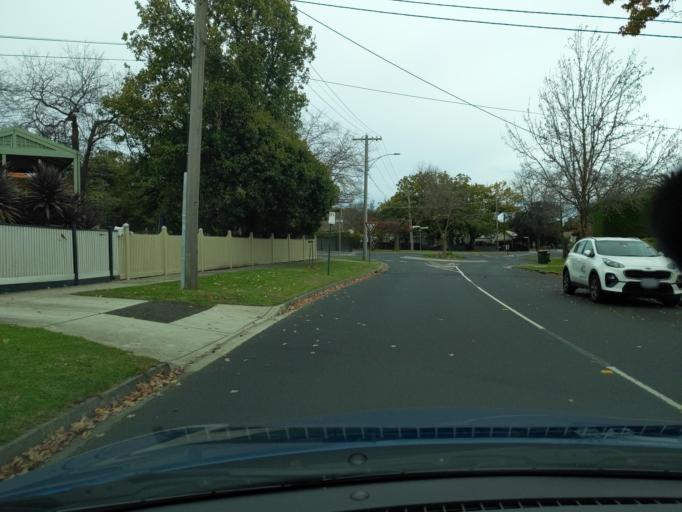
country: AU
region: Victoria
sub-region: Whitehorse
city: Surrey Hills
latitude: -37.8229
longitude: 145.1034
